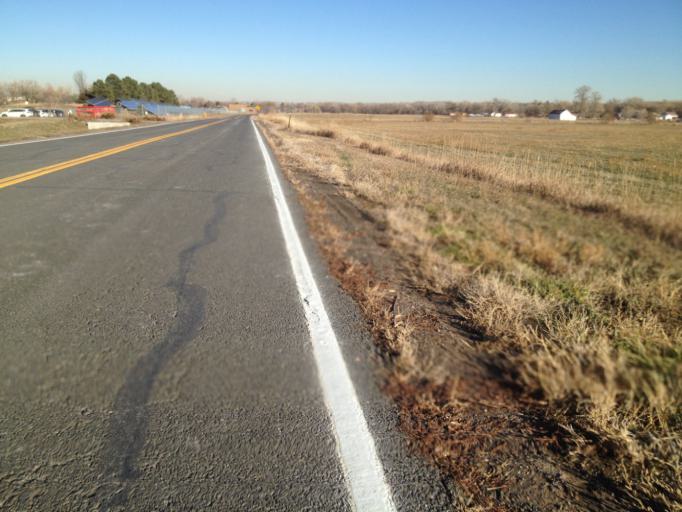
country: US
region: Colorado
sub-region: Boulder County
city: Louisville
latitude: 39.9778
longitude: -105.1248
